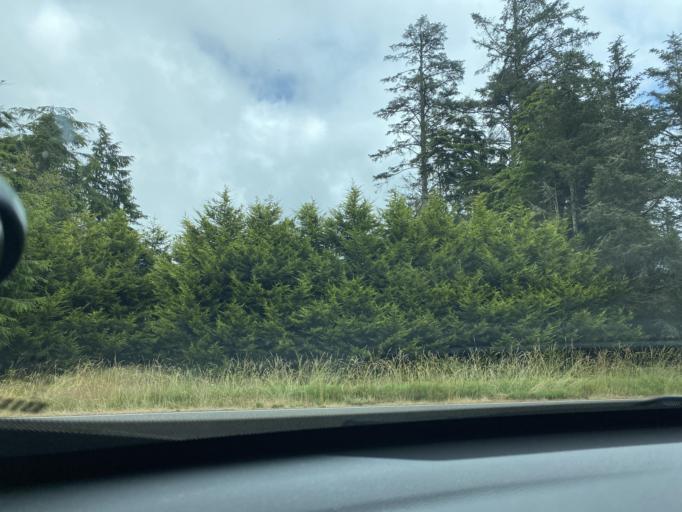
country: US
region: Washington
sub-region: Grays Harbor County
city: Ocean Shores
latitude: 46.9704
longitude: -124.1401
